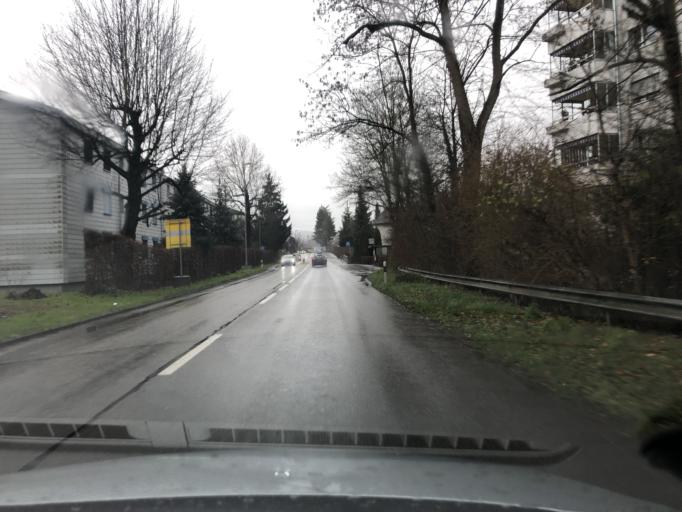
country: CH
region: Aargau
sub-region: Bezirk Brugg
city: Brugg
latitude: 47.4730
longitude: 8.2119
